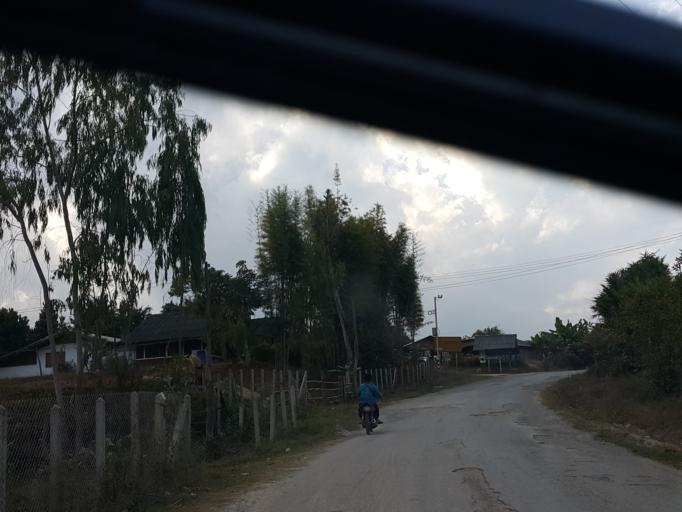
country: TH
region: Chiang Mai
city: Om Koi
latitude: 17.8013
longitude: 98.3352
